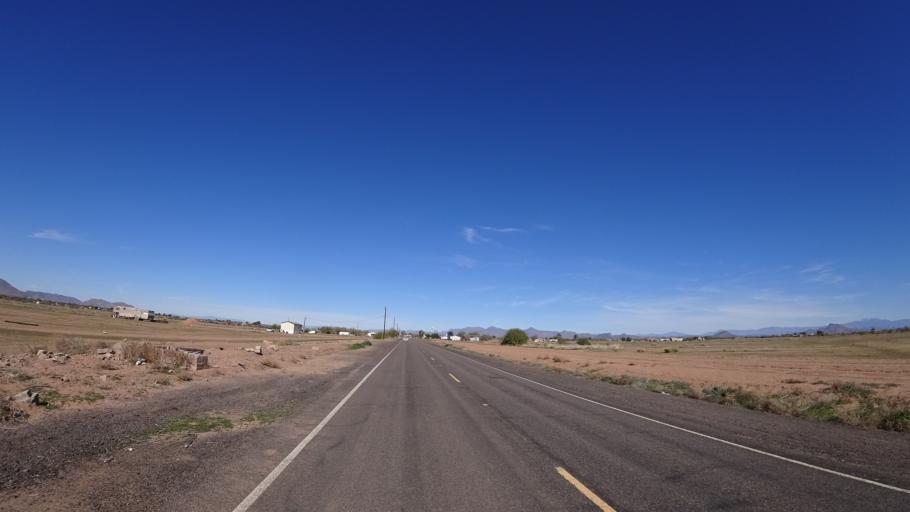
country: US
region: Arizona
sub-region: Maricopa County
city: Mesa
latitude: 33.4562
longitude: -111.8660
